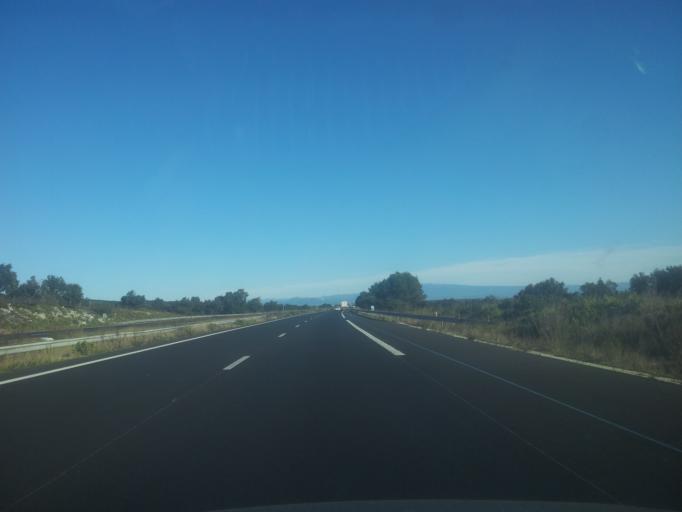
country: FR
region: Languedoc-Roussillon
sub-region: Departement du Gard
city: Rochefort-du-Gard
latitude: 43.9810
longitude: 4.6665
